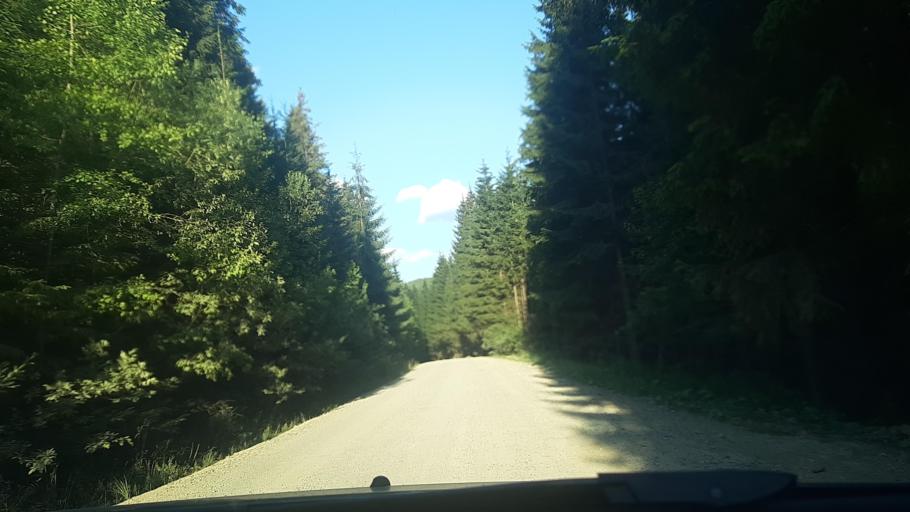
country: RO
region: Alba
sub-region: Comuna Sugag
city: Sugag
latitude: 45.5852
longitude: 23.6151
